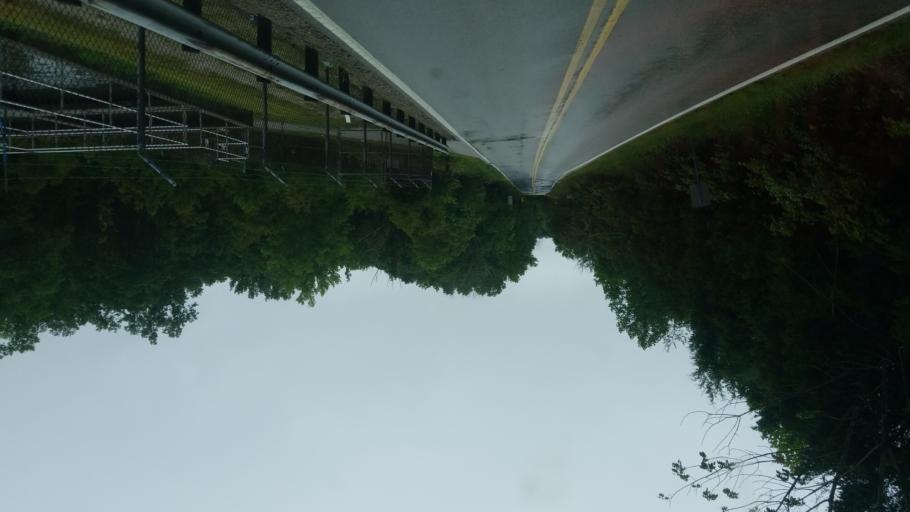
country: US
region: Ohio
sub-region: Adams County
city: West Union
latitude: 38.7889
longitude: -83.5425
